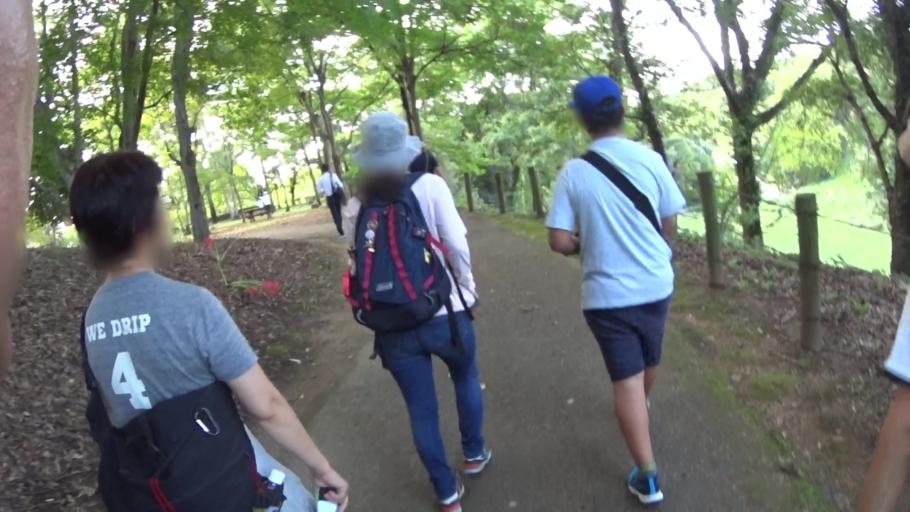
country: JP
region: Nara
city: Kashihara-shi
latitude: 34.4637
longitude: 135.8044
